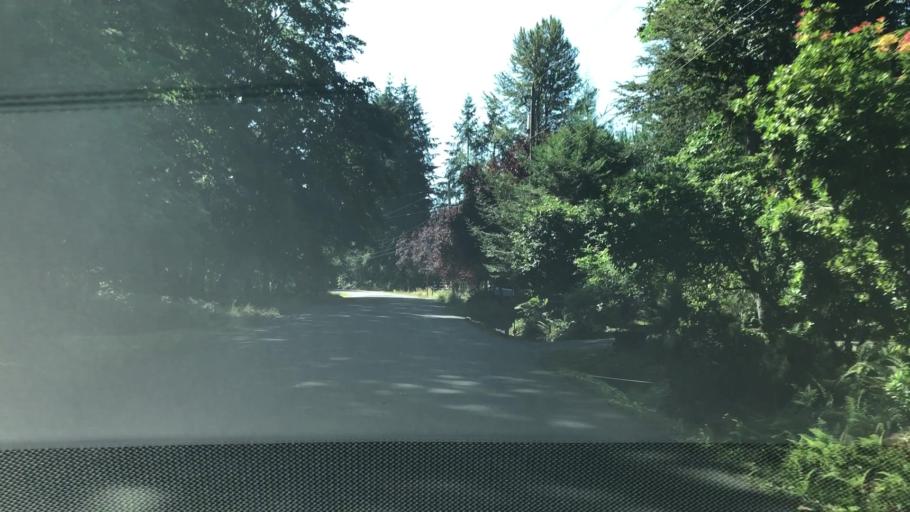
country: US
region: Washington
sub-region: King County
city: Cottage Lake
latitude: 47.7558
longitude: -122.1169
